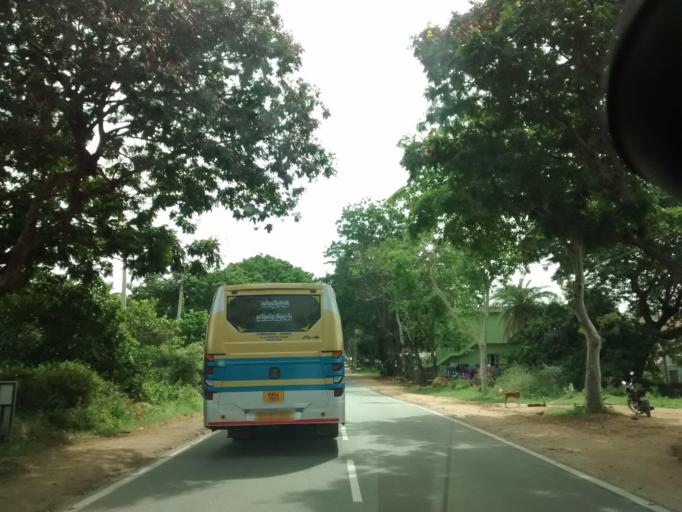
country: IN
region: Karnataka
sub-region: Tumkur
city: Koratagere
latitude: 13.5124
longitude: 77.2244
